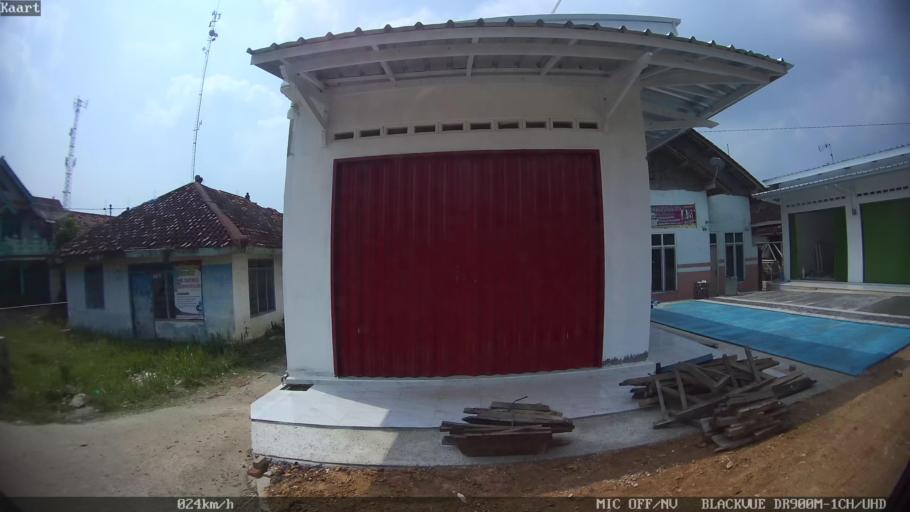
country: ID
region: Lampung
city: Gadingrejo
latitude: -5.3745
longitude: 105.0581
